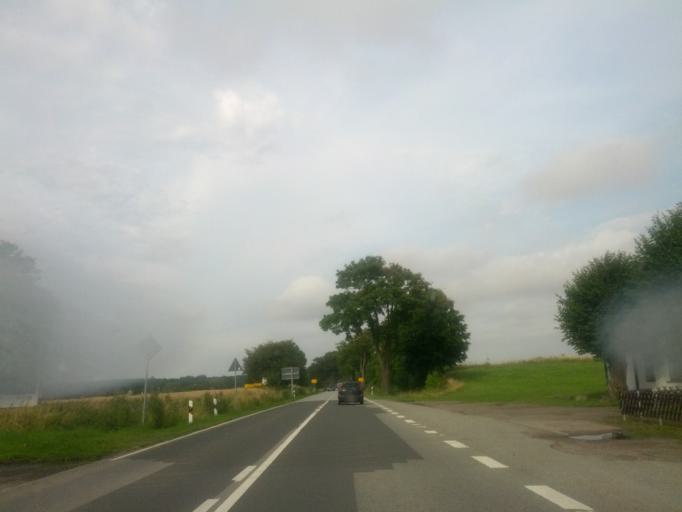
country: DE
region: Mecklenburg-Vorpommern
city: Neubukow
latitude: 53.9858
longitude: 11.6288
